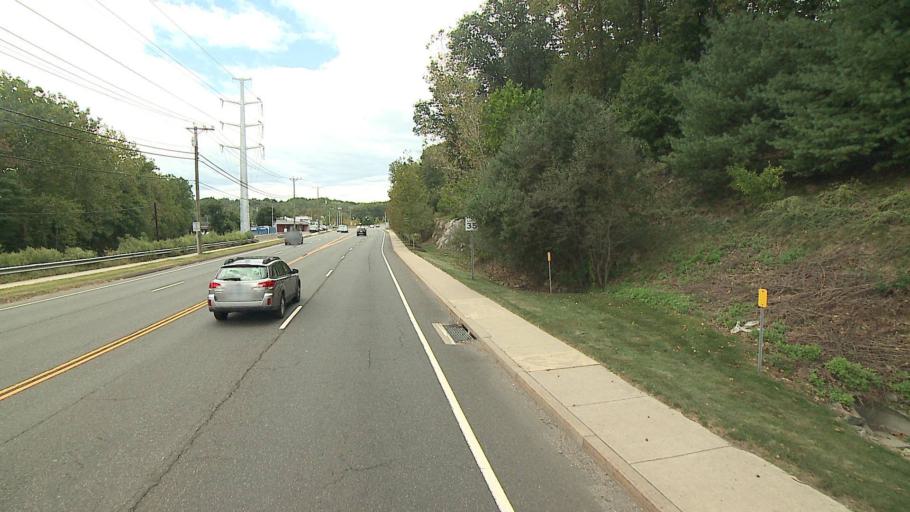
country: US
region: Connecticut
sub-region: Fairfield County
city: Wilton
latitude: 41.1936
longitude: -73.4296
